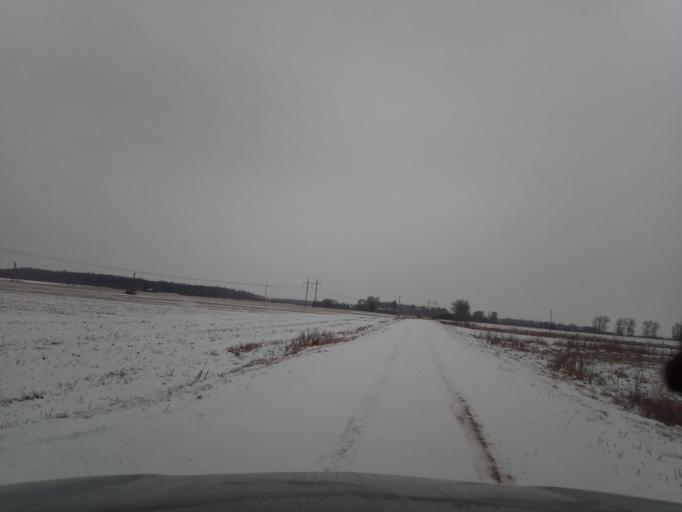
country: LT
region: Panevezys
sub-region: Panevezys City
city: Panevezys
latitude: 55.6260
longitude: 24.3386
